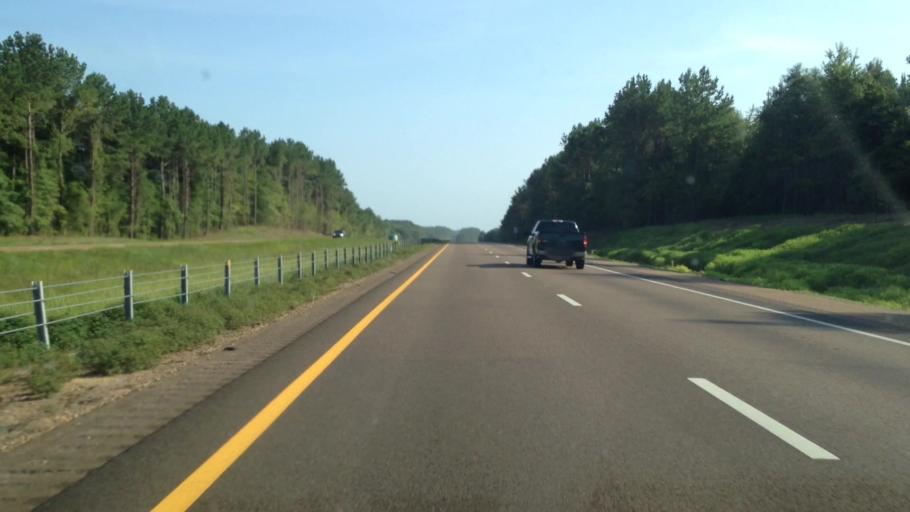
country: US
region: Mississippi
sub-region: Pike County
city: Summit
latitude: 31.4301
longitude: -90.4797
